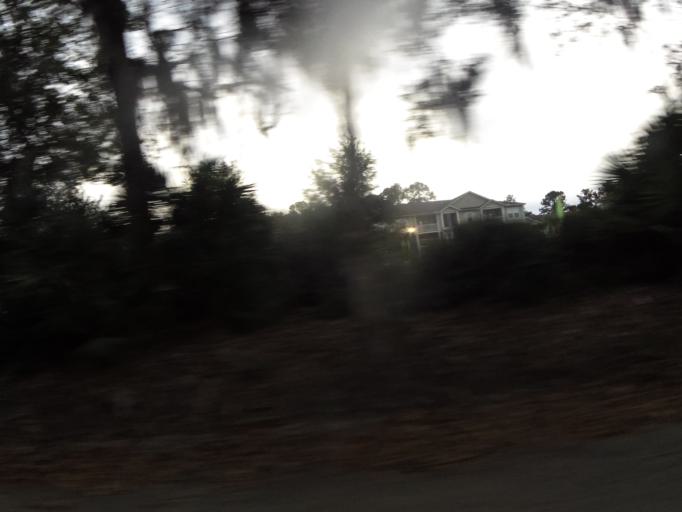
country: US
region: Florida
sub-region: Duval County
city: Jacksonville
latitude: 30.2424
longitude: -81.5825
